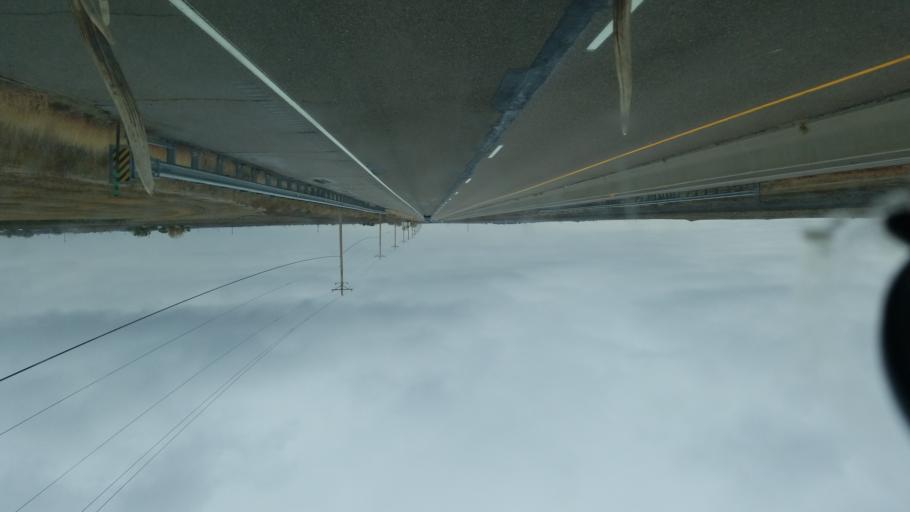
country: US
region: Colorado
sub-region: Pueblo County
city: Pueblo
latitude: 38.2729
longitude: -104.4393
